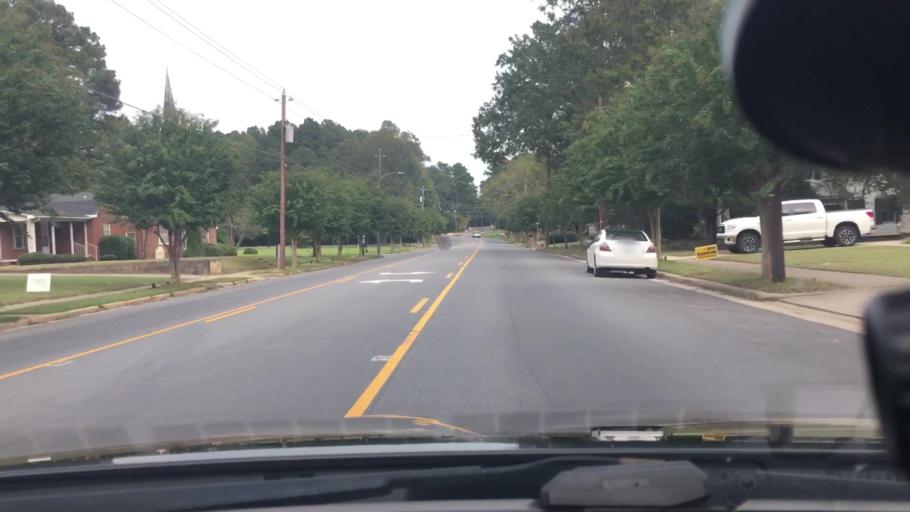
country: US
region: North Carolina
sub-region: Montgomery County
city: Troy
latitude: 35.3585
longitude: -79.8906
